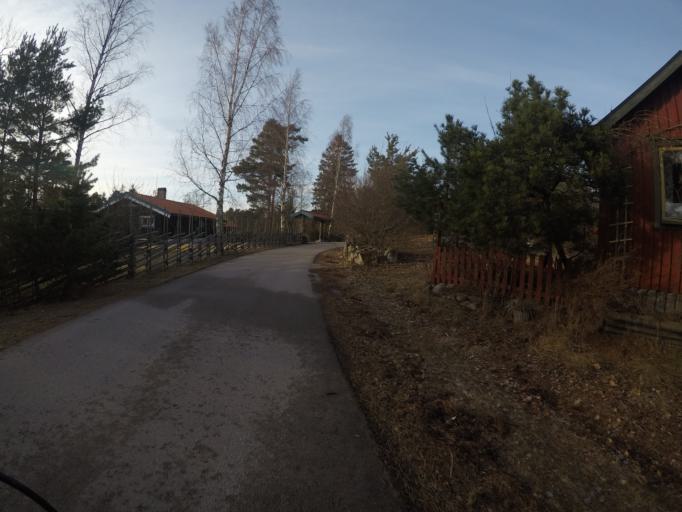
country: SE
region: Soedermanland
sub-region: Eskilstuna Kommun
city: Kvicksund
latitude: 59.4606
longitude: 16.2972
